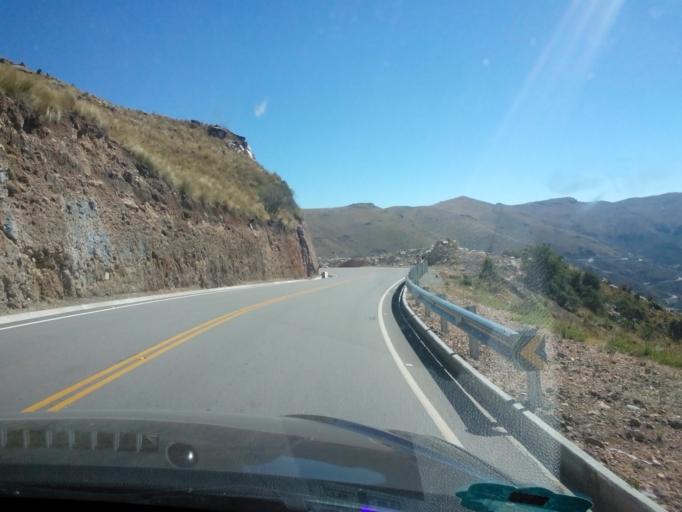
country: PE
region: Ayacucho
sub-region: Provincia de Huamanga
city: Ocros
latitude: -13.3942
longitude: -73.9498
